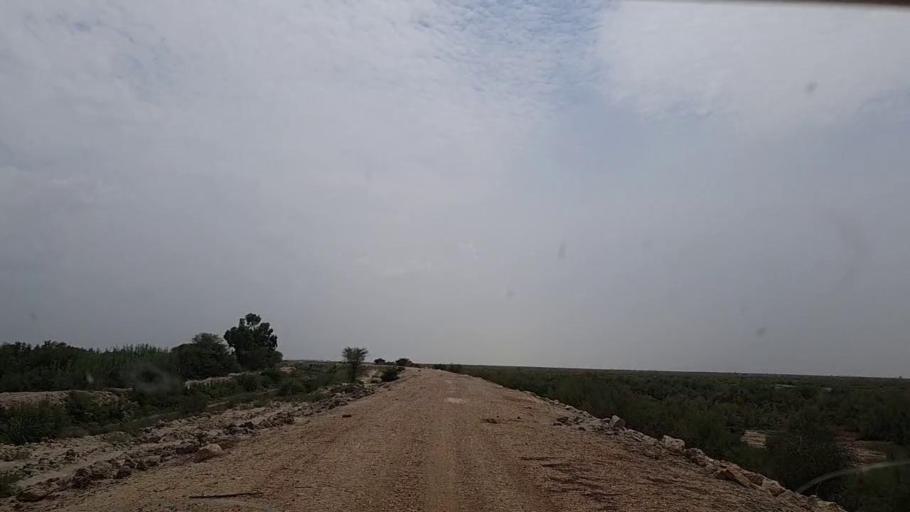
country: PK
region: Sindh
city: Phulji
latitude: 26.8476
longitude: 67.6199
